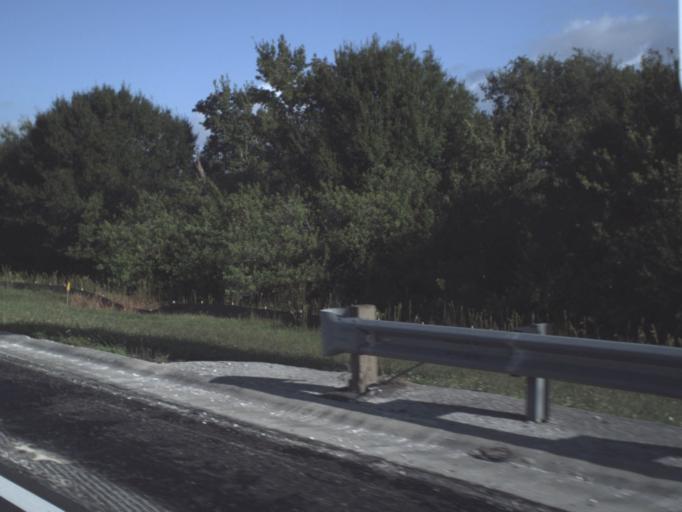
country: US
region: Florida
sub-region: Osceola County
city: Saint Cloud
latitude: 28.0431
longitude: -81.2094
